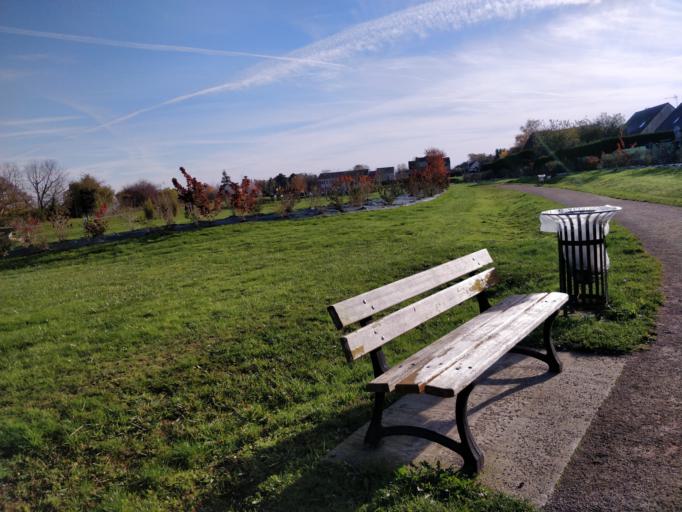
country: FR
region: Ile-de-France
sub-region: Departement de l'Essonne
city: Limours
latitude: 48.6424
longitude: 2.0677
